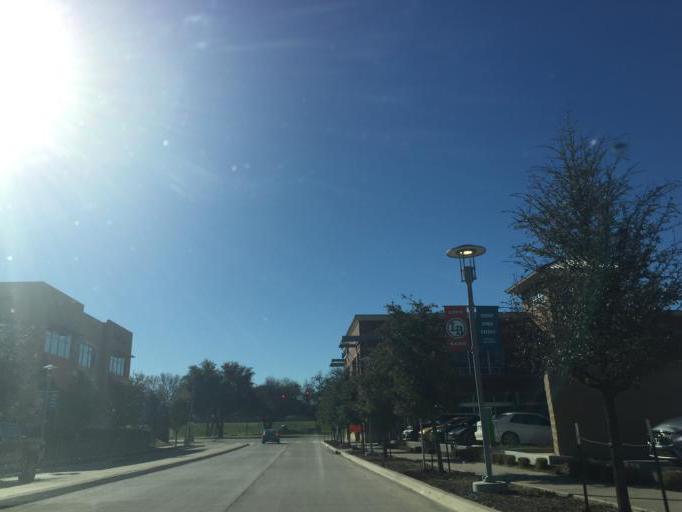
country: US
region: Texas
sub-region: Tarrant County
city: Fort Worth
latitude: 32.7519
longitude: -97.3490
